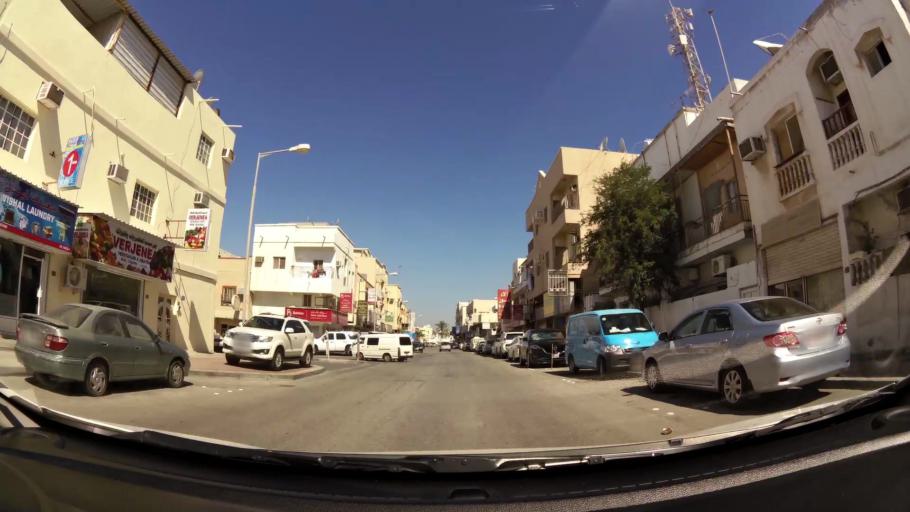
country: BH
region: Muharraq
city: Al Muharraq
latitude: 26.2569
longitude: 50.6191
